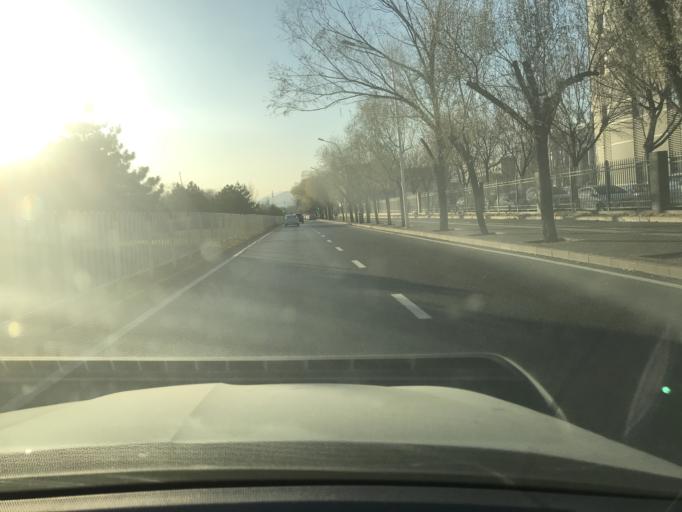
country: CN
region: Beijing
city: Xibeiwang
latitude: 40.0676
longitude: 116.2459
